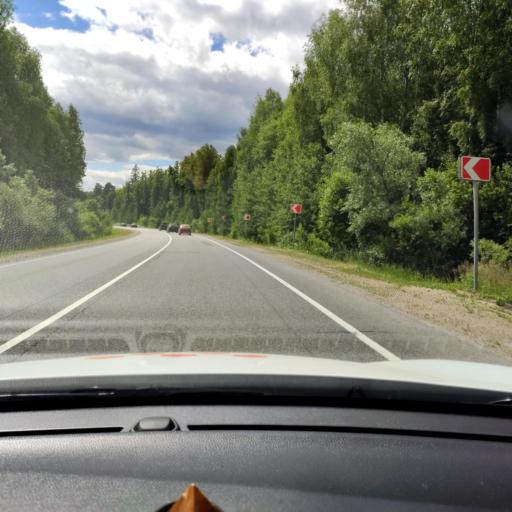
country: RU
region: Tatarstan
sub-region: Zelenodol'skiy Rayon
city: Zelenodolsk
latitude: 55.8982
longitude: 48.5520
